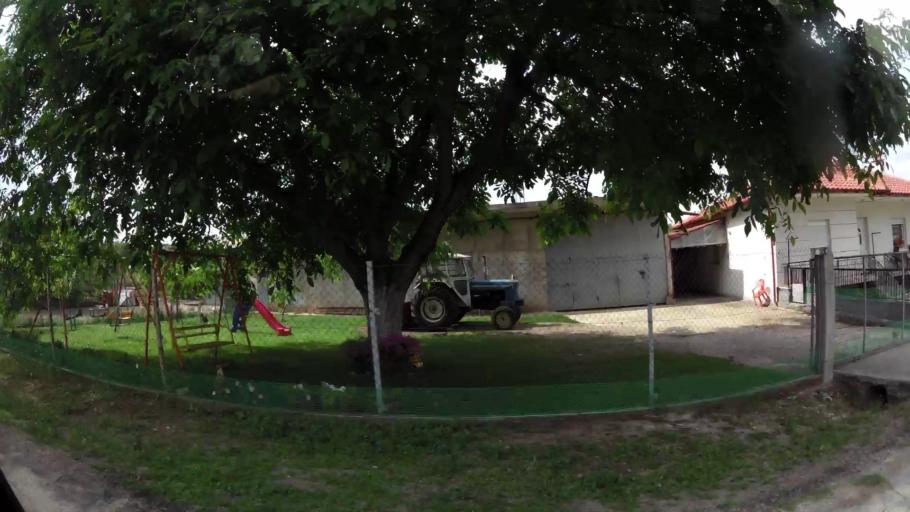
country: GR
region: West Macedonia
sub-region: Nomos Kozanis
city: Koila
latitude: 40.3480
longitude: 21.8251
